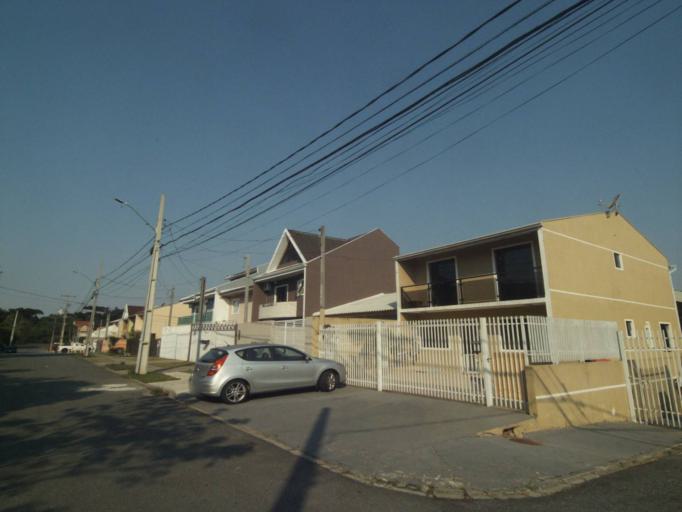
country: BR
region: Parana
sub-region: Curitiba
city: Curitiba
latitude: -25.4904
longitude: -49.2652
